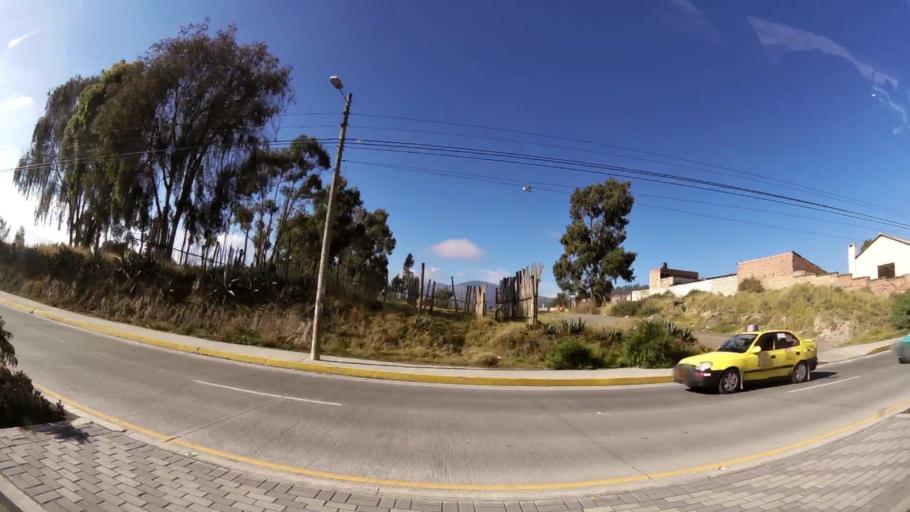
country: EC
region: Chimborazo
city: Riobamba
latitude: -1.6634
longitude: -78.6706
